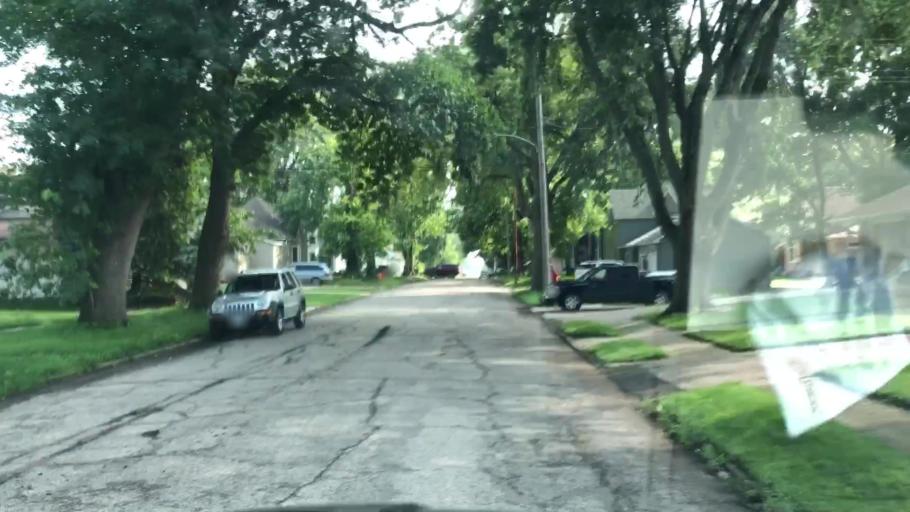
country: US
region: Iowa
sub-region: O'Brien County
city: Sheldon
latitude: 43.1792
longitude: -95.8482
